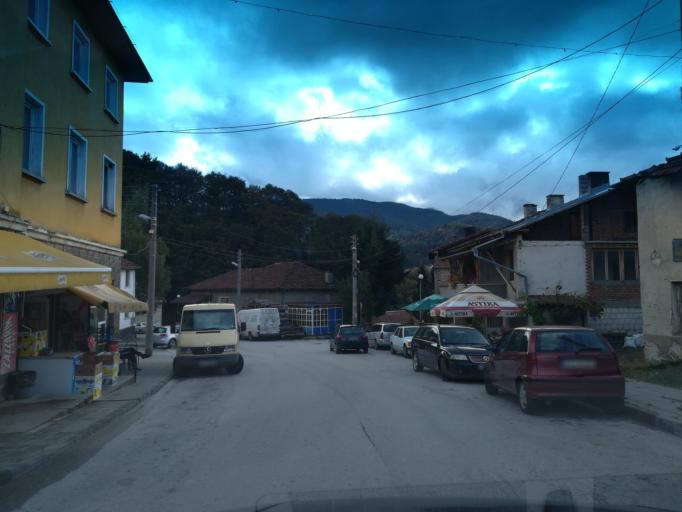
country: BG
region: Pazardzhik
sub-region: Obshtina Batak
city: Batak
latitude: 41.9372
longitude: 24.2707
